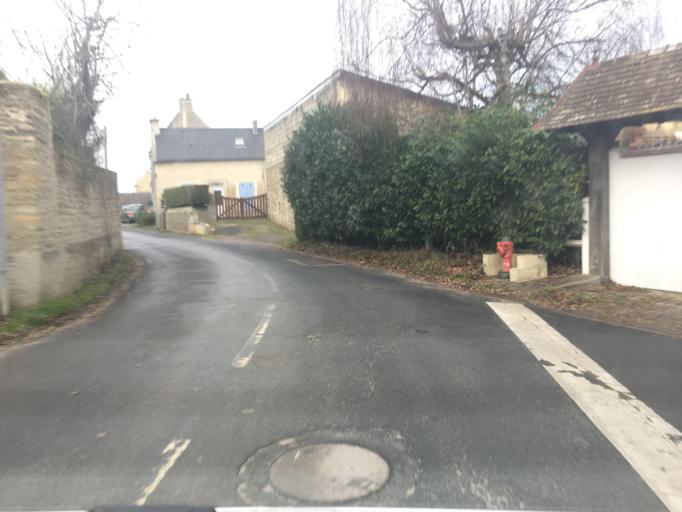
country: FR
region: Lower Normandy
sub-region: Departement du Calvados
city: Saint-Vigor-le-Grand
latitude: 49.3363
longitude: -0.6416
